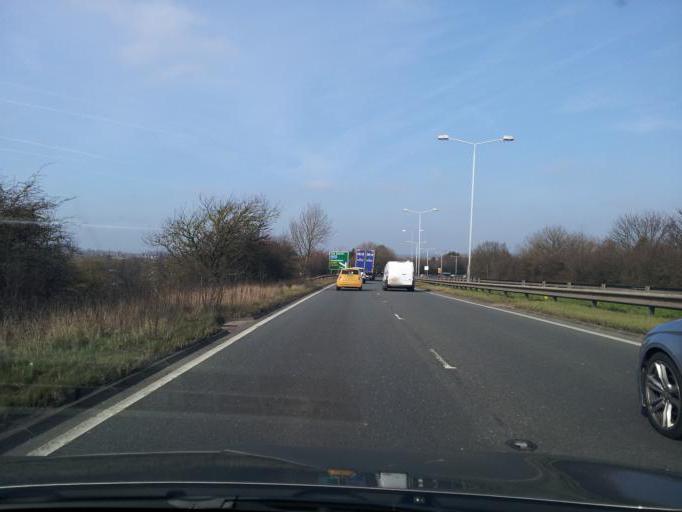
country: GB
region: England
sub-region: Nottinghamshire
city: Ruddington
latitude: 52.9120
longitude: -1.1566
